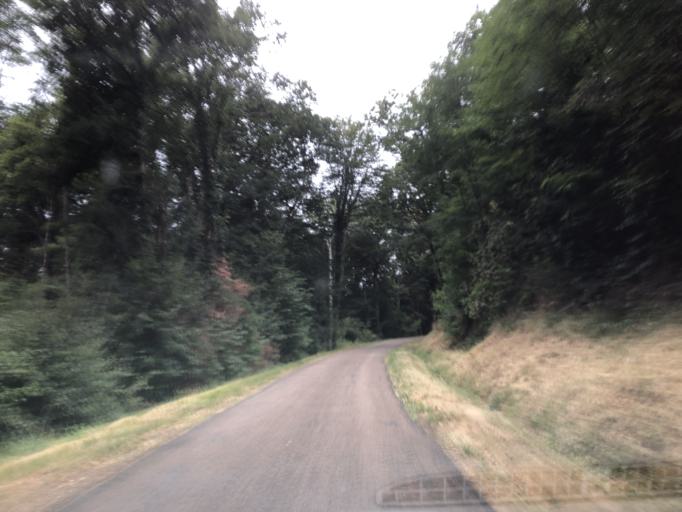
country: FR
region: Bourgogne
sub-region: Departement de l'Yonne
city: Aillant-sur-Tholon
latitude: 47.9009
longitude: 3.3166
